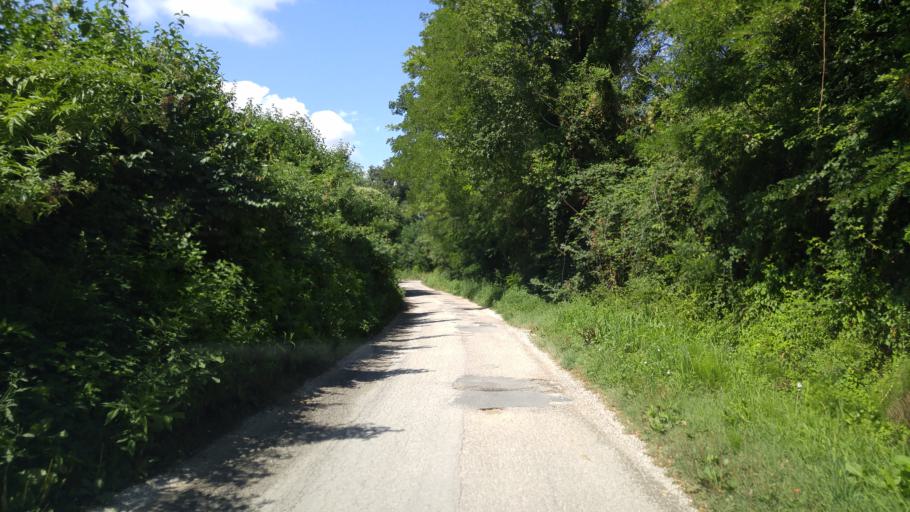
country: IT
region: The Marches
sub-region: Provincia di Pesaro e Urbino
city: Centinarola
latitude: 43.8298
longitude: 12.9803
